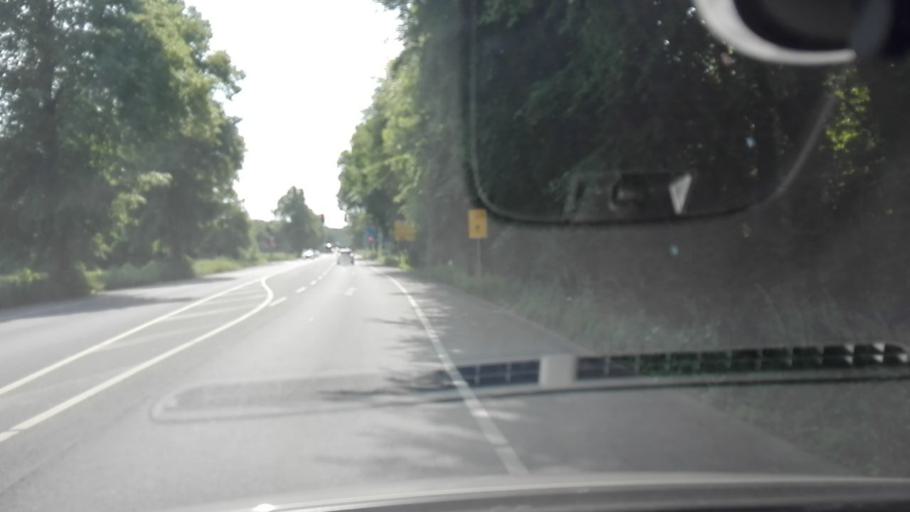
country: DE
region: North Rhine-Westphalia
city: Bergkamen
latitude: 51.5958
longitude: 7.6125
